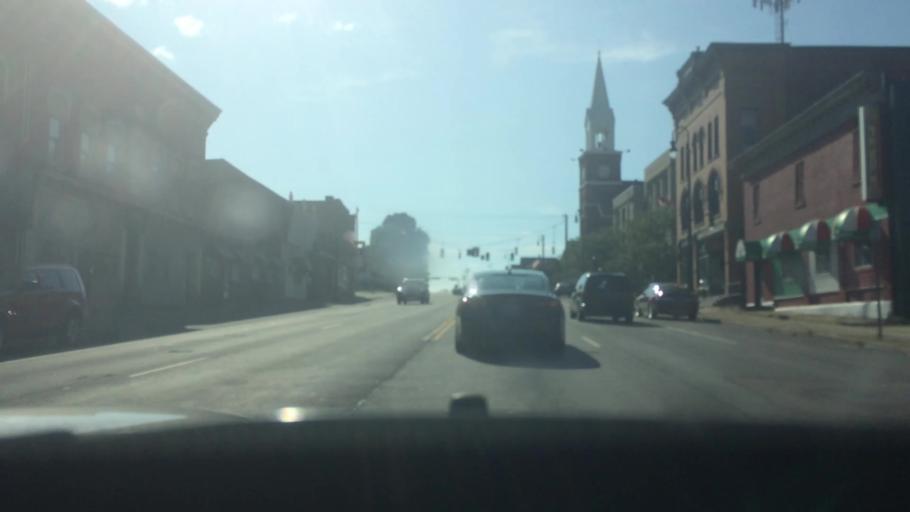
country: US
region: New York
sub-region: Franklin County
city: Malone
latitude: 44.8489
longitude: -74.2942
